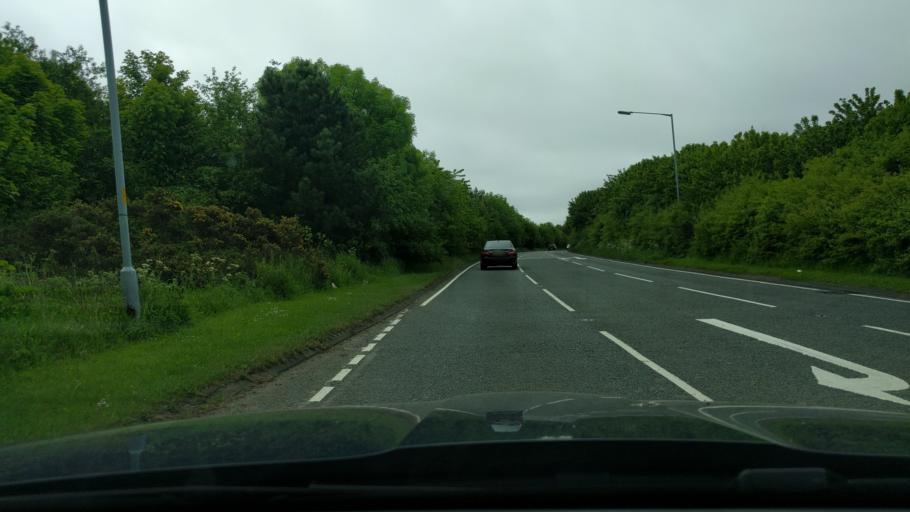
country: GB
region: England
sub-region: Northumberland
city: Cresswell
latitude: 55.2159
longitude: -1.5706
